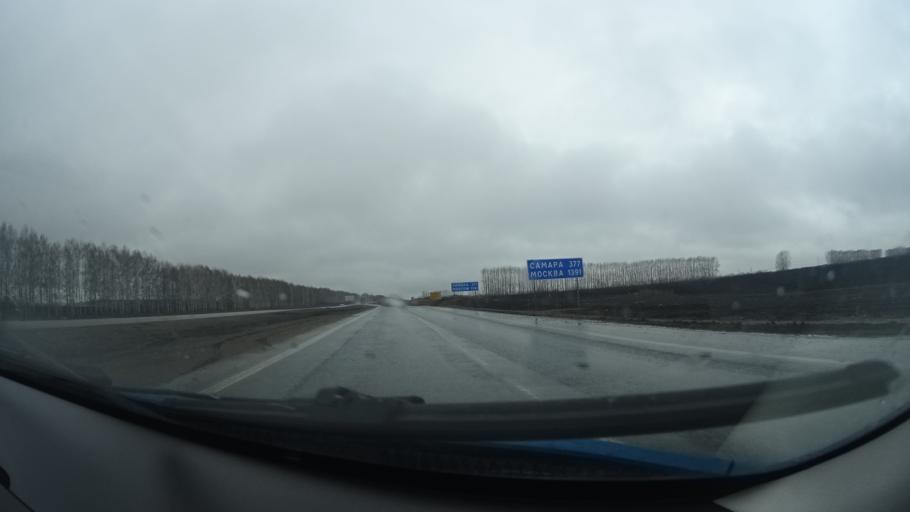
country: RU
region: Bashkortostan
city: Buzdyak
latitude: 54.7064
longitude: 54.8625
